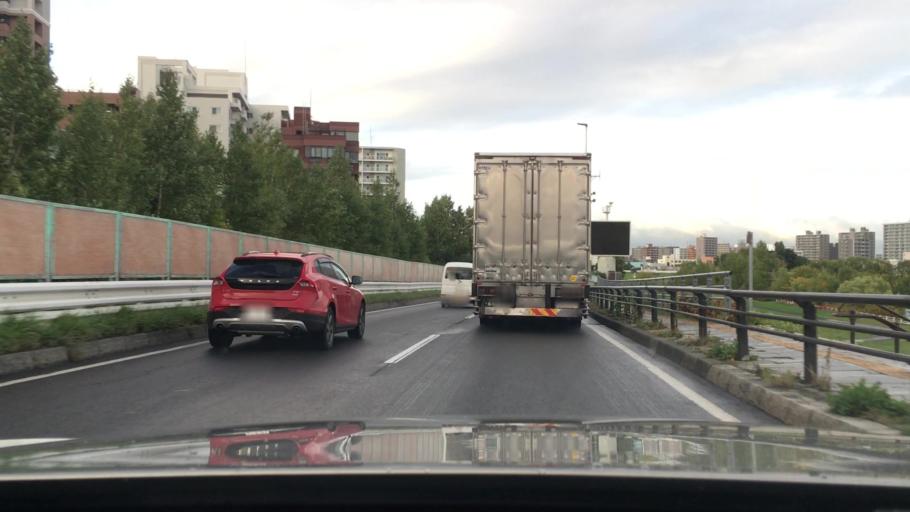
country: JP
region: Hokkaido
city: Sapporo
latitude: 43.0402
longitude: 141.3570
